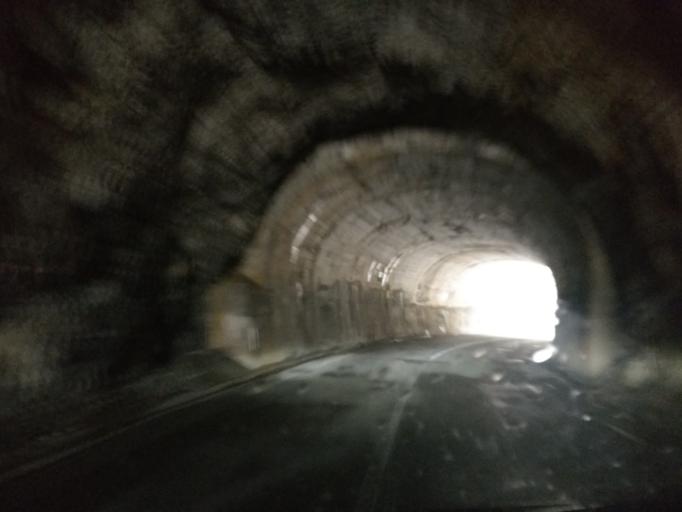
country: ME
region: Opstina Pluzine
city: Pluzine
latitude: 43.2341
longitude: 18.8457
